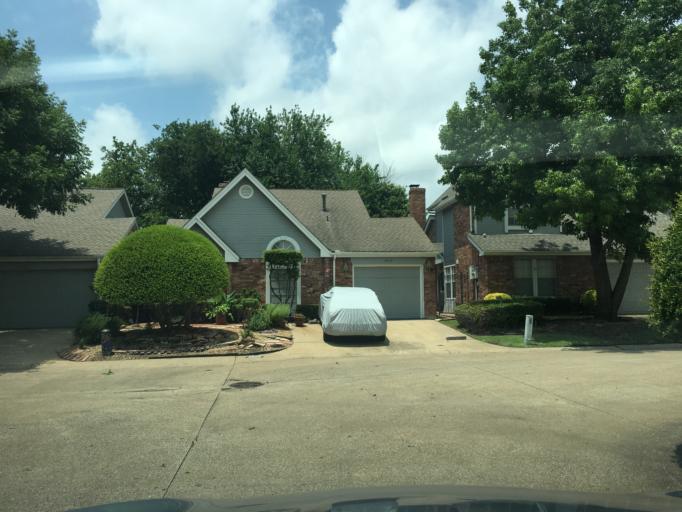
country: US
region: Texas
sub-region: Dallas County
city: Garland
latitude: 32.9304
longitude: -96.6746
